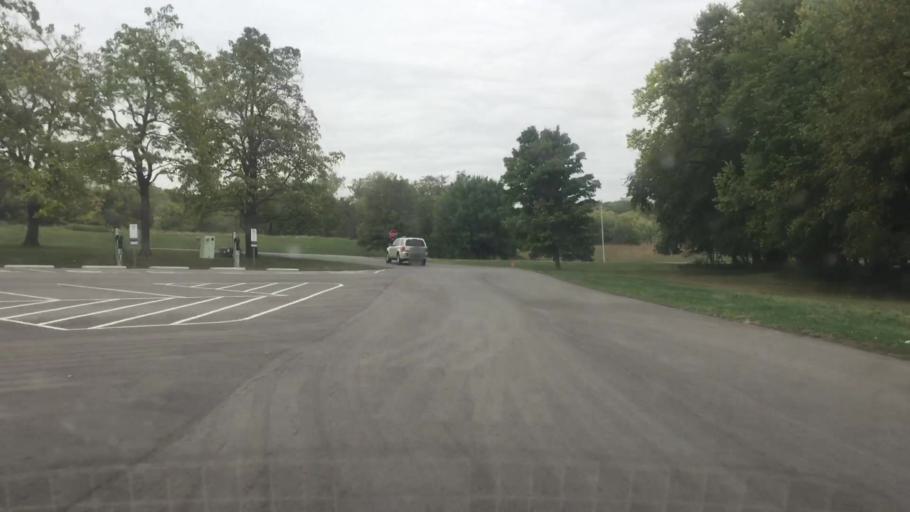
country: US
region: Kansas
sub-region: Johnson County
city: Lenexa
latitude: 38.9877
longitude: -94.7995
